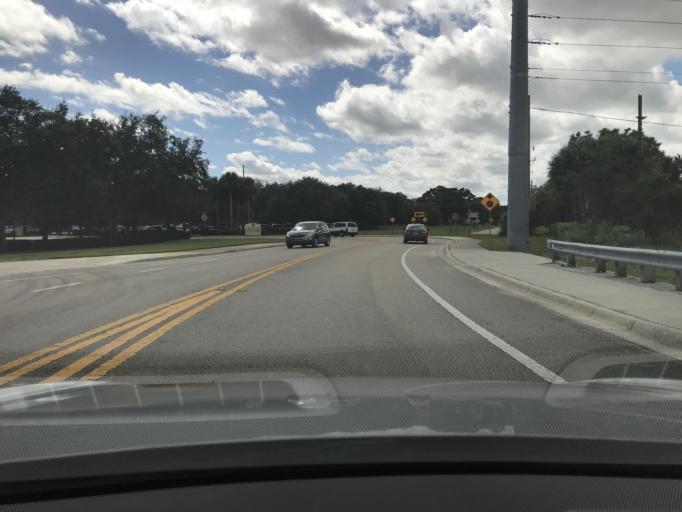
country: US
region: Florida
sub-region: Indian River County
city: Vero Beach
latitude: 27.6474
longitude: -80.4057
